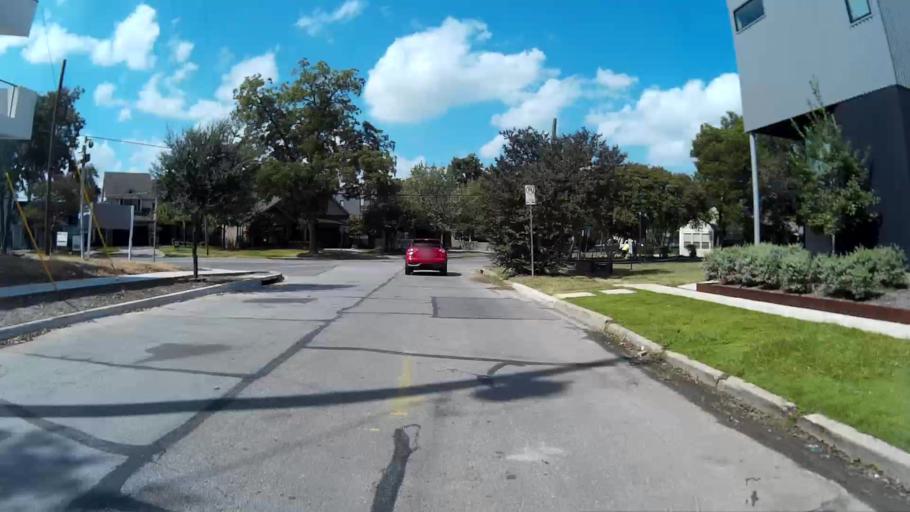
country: US
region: Texas
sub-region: Dallas County
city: Highland Park
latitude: 32.8154
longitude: -96.7770
